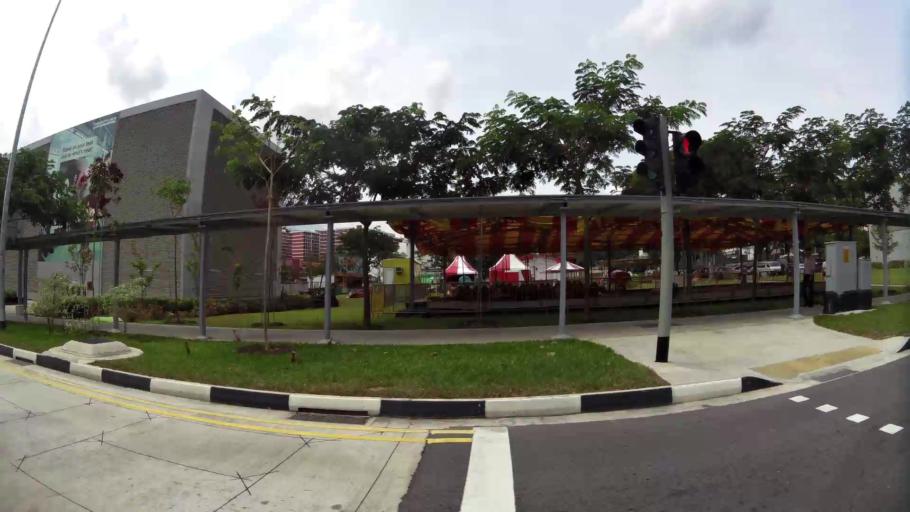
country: SG
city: Singapore
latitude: 1.3413
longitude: 103.7757
